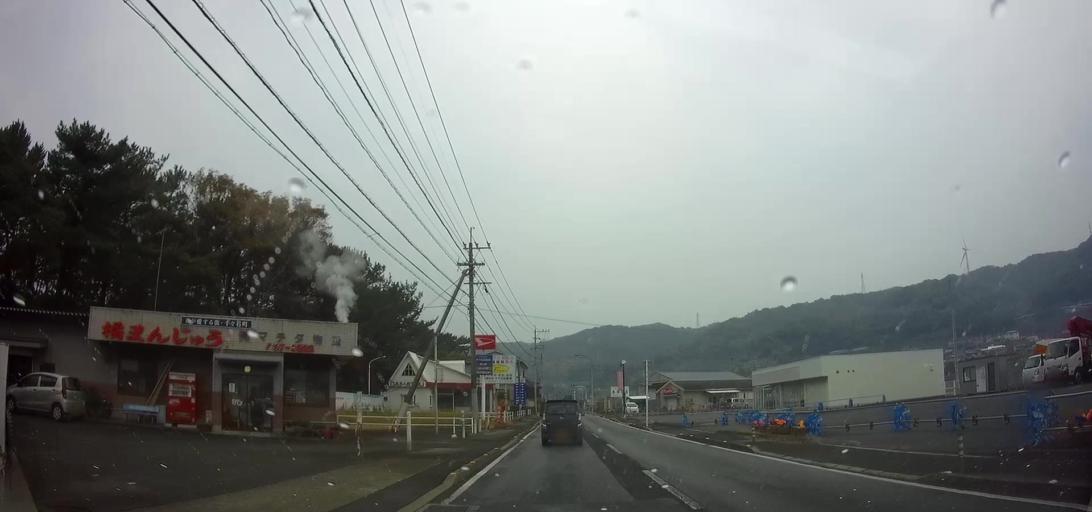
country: JP
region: Nagasaki
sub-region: Isahaya-shi
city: Isahaya
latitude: 32.7906
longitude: 130.1869
